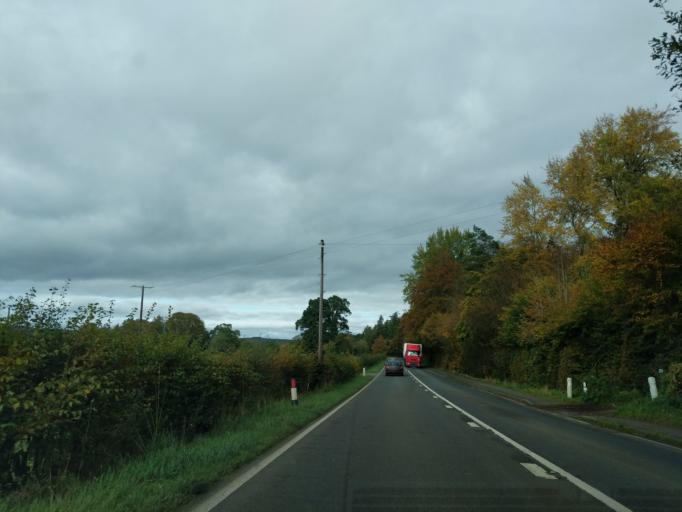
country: GB
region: Scotland
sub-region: Dumfries and Galloway
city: Thornhill
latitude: 55.2541
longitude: -3.7743
